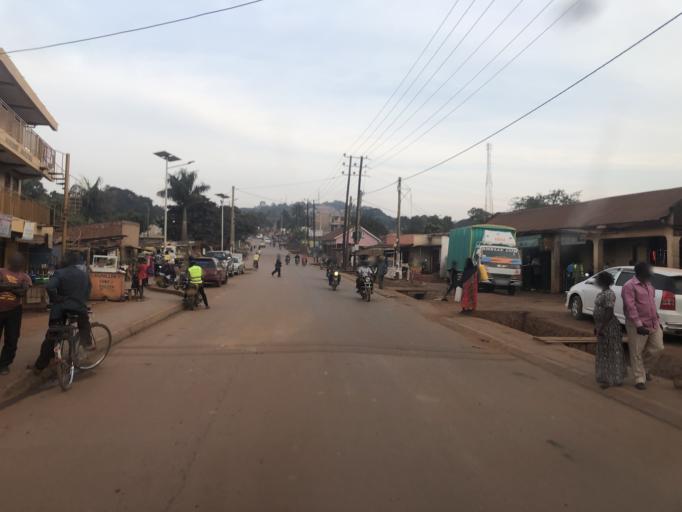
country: UG
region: Central Region
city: Kampala Central Division
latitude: 0.2962
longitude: 32.5271
